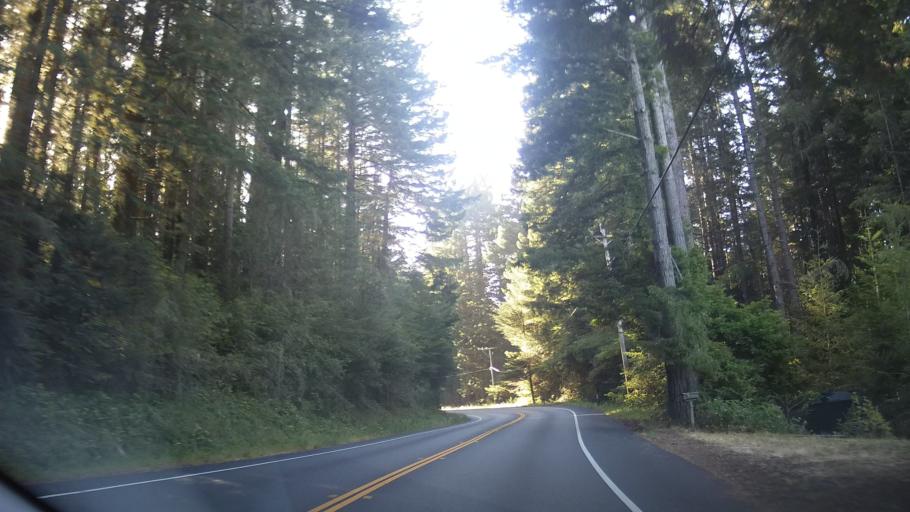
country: US
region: California
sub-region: Mendocino County
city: Fort Bragg
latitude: 39.4040
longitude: -123.7205
